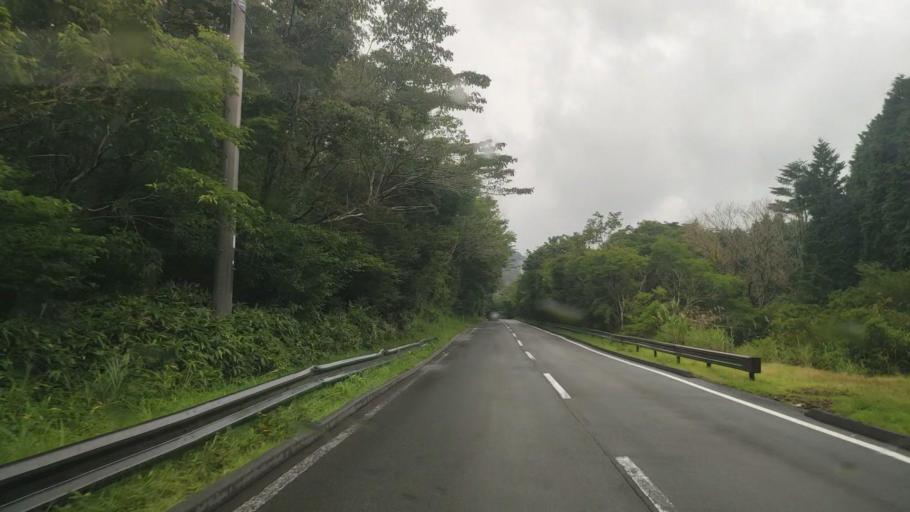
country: JP
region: Shizuoka
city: Gotemba
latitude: 35.2795
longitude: 138.7944
